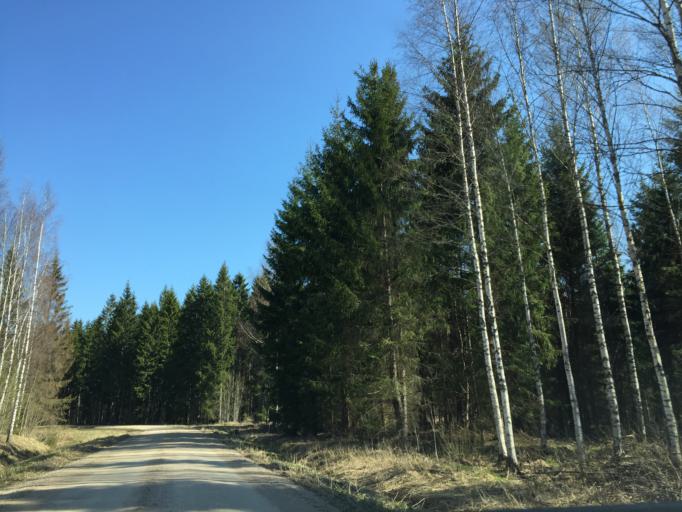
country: EE
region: Tartu
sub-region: Alatskivi vald
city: Kallaste
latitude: 58.5570
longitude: 26.9385
